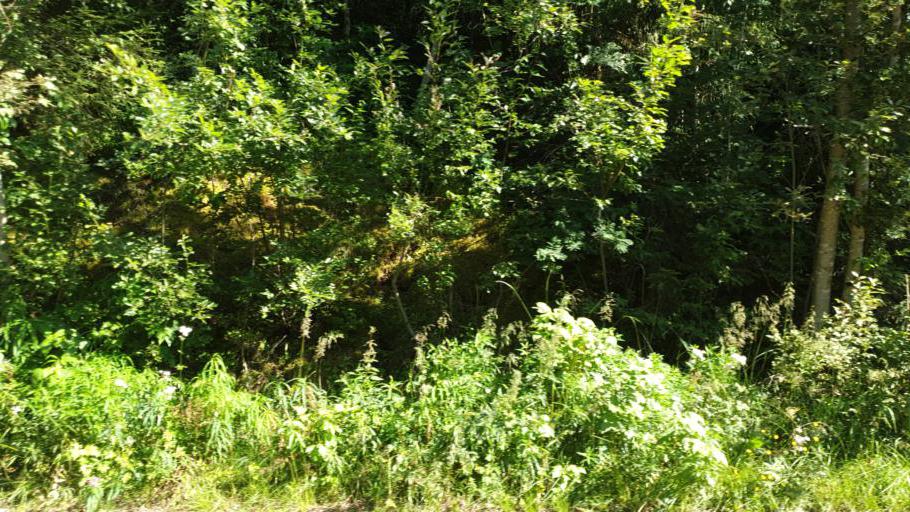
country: NO
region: Sor-Trondelag
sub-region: Orkdal
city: Orkanger
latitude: 63.1900
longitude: 9.7802
